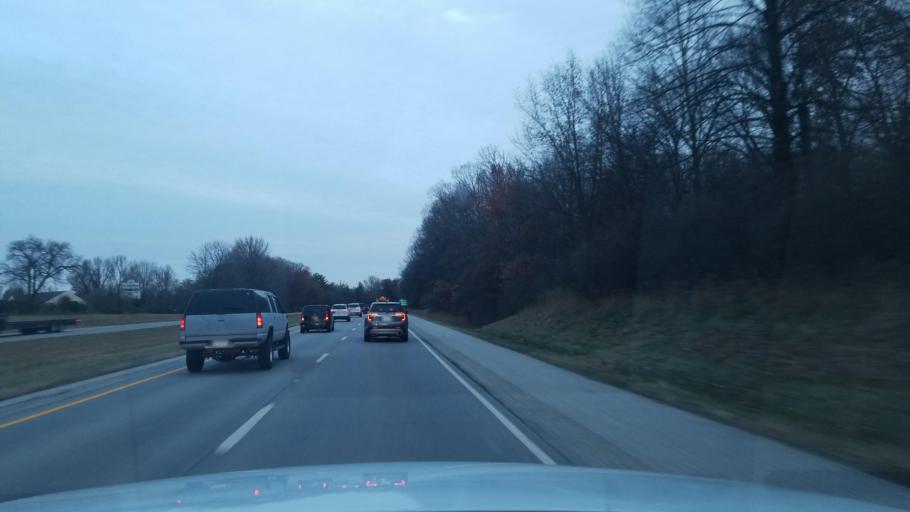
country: US
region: Indiana
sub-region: Vanderburgh County
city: Evansville
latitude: 37.9603
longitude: -87.6915
